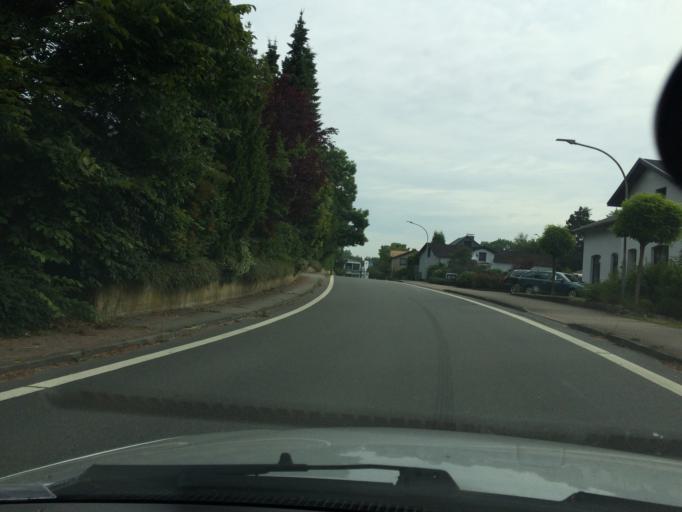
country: DE
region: Schleswig-Holstein
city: Oeversee
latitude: 54.7035
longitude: 9.4347
